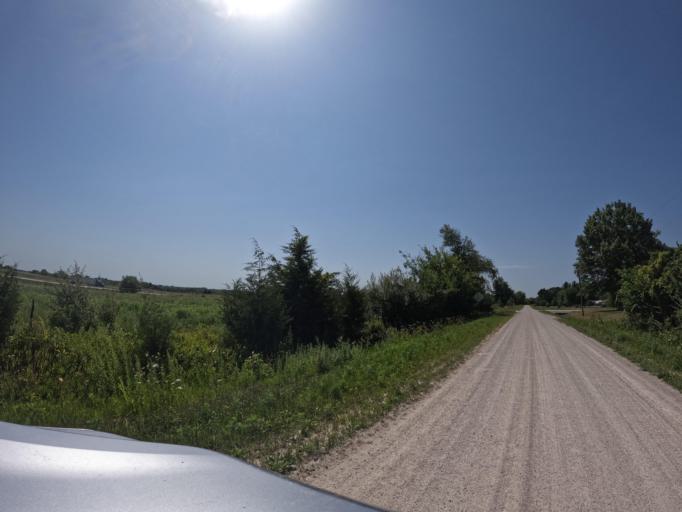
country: US
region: Iowa
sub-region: Henry County
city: Mount Pleasant
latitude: 40.9356
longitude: -91.5380
